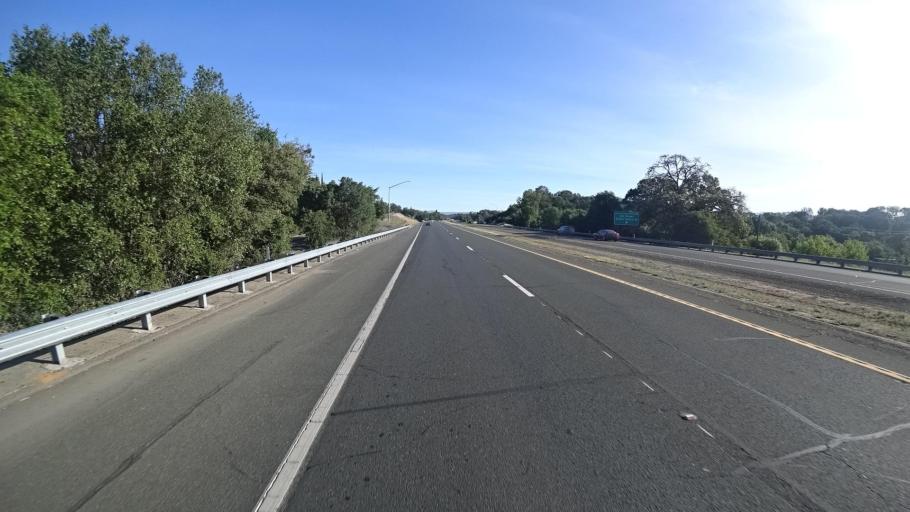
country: US
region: California
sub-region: Lake County
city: Lakeport
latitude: 39.0458
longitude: -122.9317
